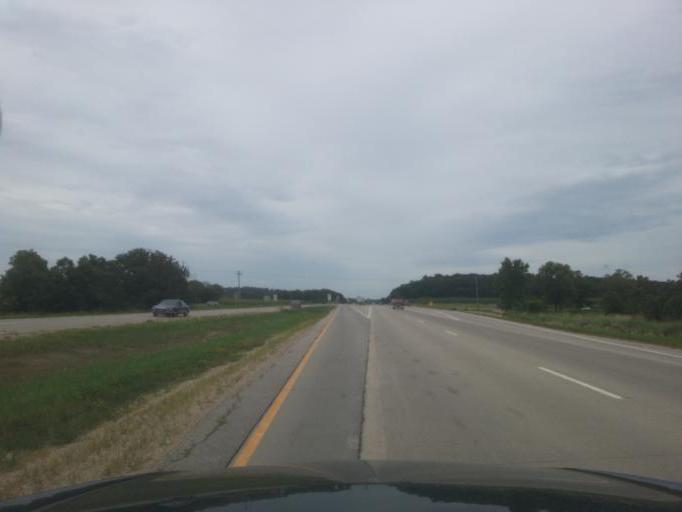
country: US
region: Wisconsin
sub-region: Dane County
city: McFarland
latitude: 43.0412
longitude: -89.2496
